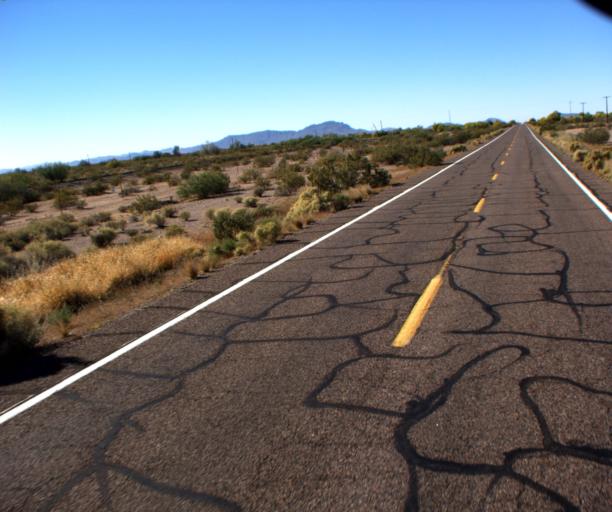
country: US
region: Arizona
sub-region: Maricopa County
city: Gila Bend
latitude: 32.8875
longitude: -112.7504
